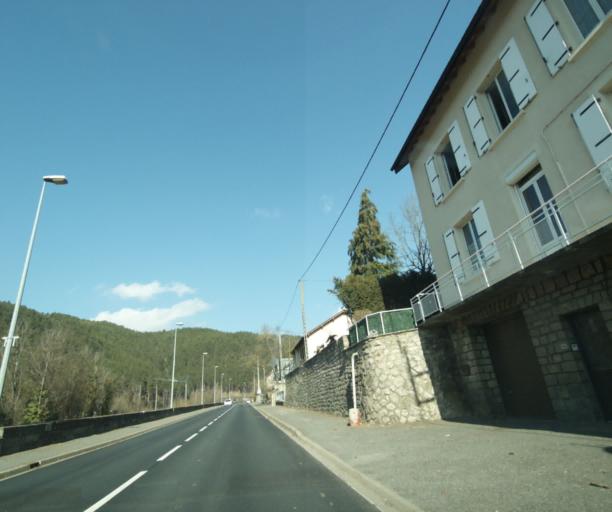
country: FR
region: Languedoc-Roussillon
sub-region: Departement de la Lozere
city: Mende
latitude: 44.5236
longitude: 3.5106
